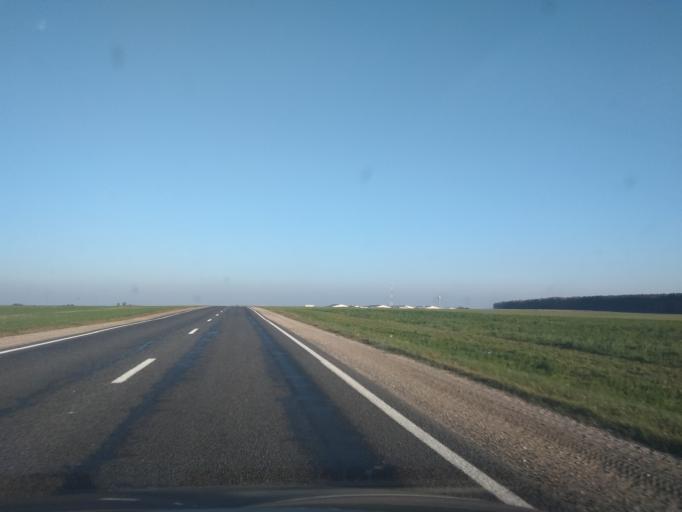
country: BY
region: Grodnenskaya
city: Svislach
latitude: 53.1299
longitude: 24.1628
